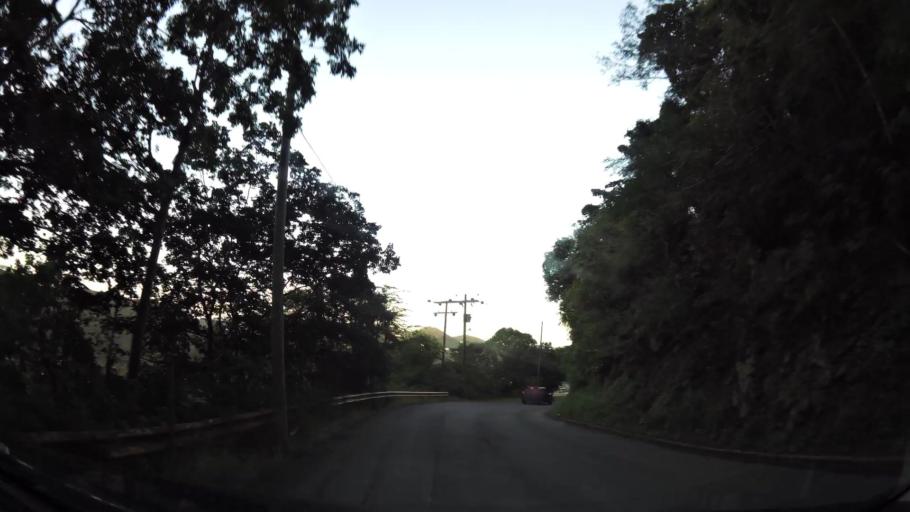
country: VG
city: Tortola
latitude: 18.4366
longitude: -64.5822
